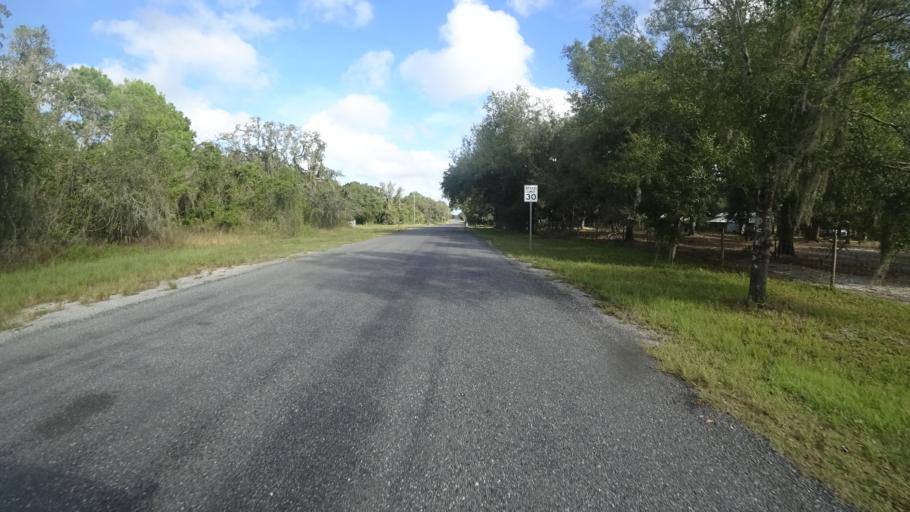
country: US
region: Florida
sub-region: Hillsborough County
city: Wimauma
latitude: 27.4600
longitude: -82.1530
